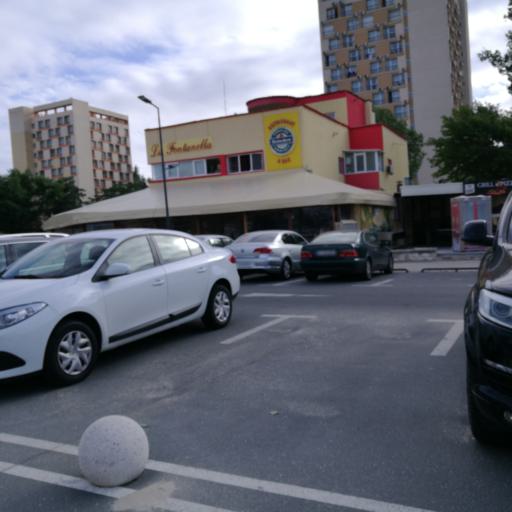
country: RO
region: Constanta
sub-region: Municipiul Constanta
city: Palazu Mare
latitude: 44.2404
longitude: 28.6241
